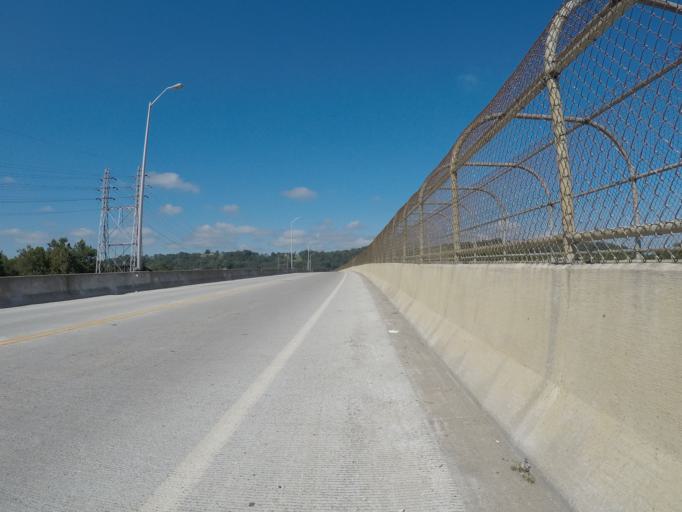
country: US
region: Kentucky
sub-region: Boyd County
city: Catlettsburg
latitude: 38.4045
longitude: -82.5936
